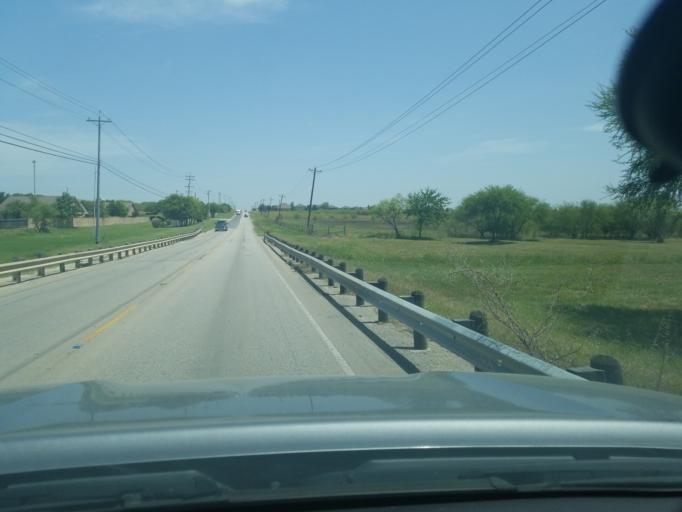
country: US
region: Texas
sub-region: Guadalupe County
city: Northcliff
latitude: 29.5932
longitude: -98.2170
